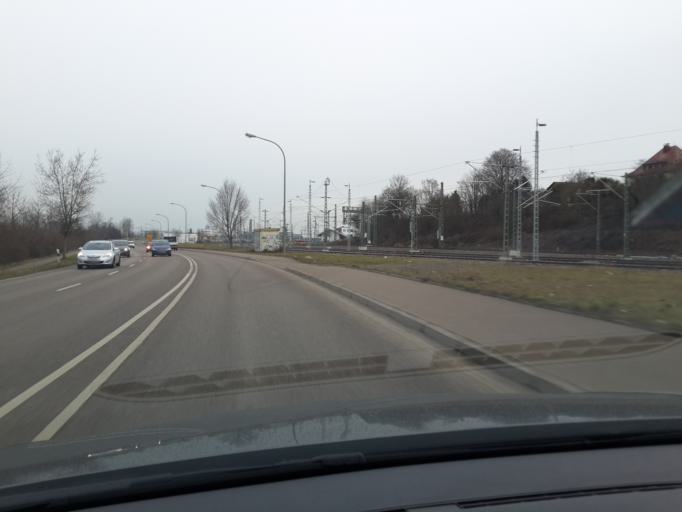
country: DE
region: Baden-Wuerttemberg
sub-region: Regierungsbezirk Stuttgart
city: Neckarsulm
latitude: 49.1845
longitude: 9.2180
